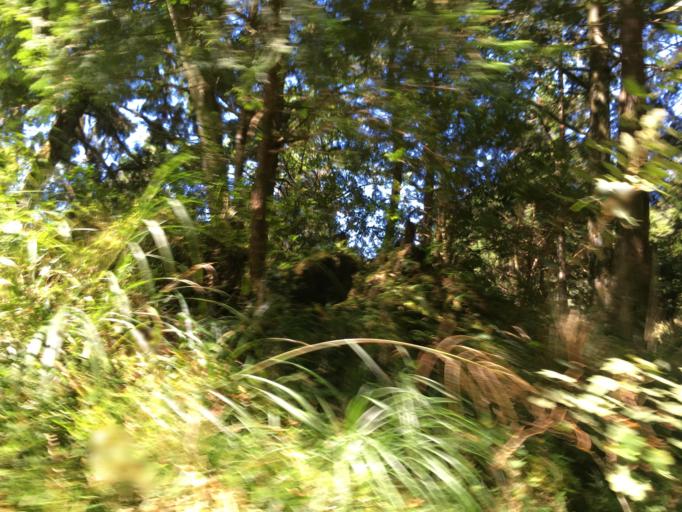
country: TW
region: Taiwan
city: Daxi
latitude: 24.5687
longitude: 121.4129
